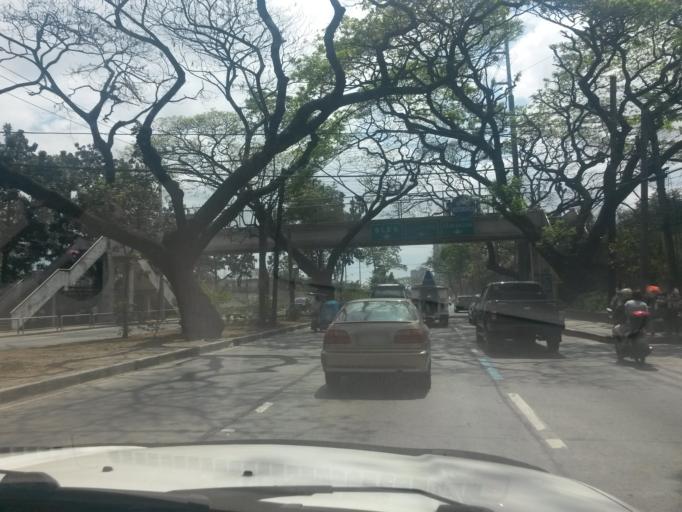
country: PH
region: Metro Manila
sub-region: Quezon City
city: Quezon City
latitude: 14.6528
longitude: 121.0743
